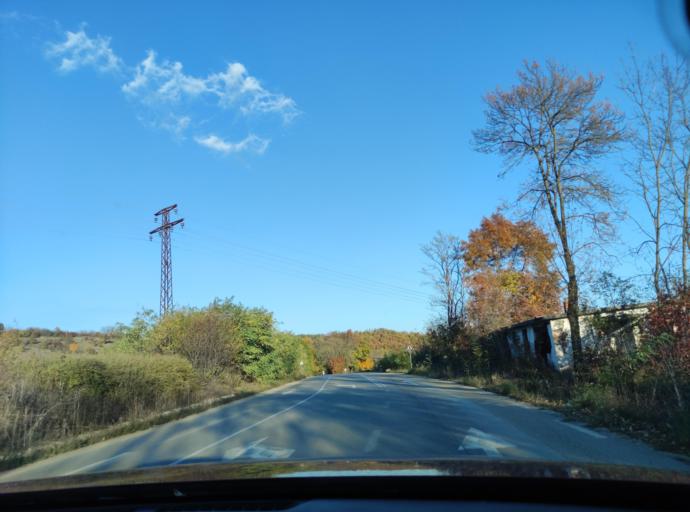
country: BG
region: Montana
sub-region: Obshtina Montana
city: Montana
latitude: 43.3978
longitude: 23.1071
